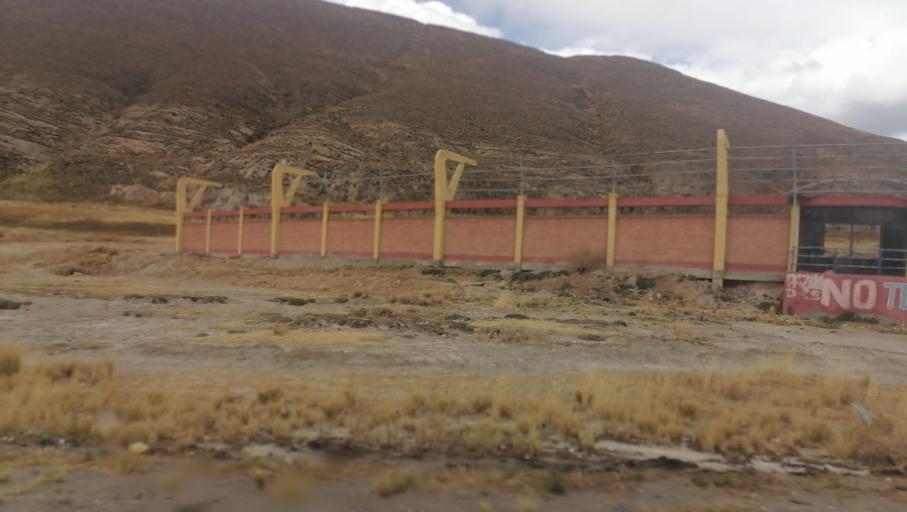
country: BO
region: Oruro
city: Totoral
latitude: -18.5916
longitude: -66.9265
